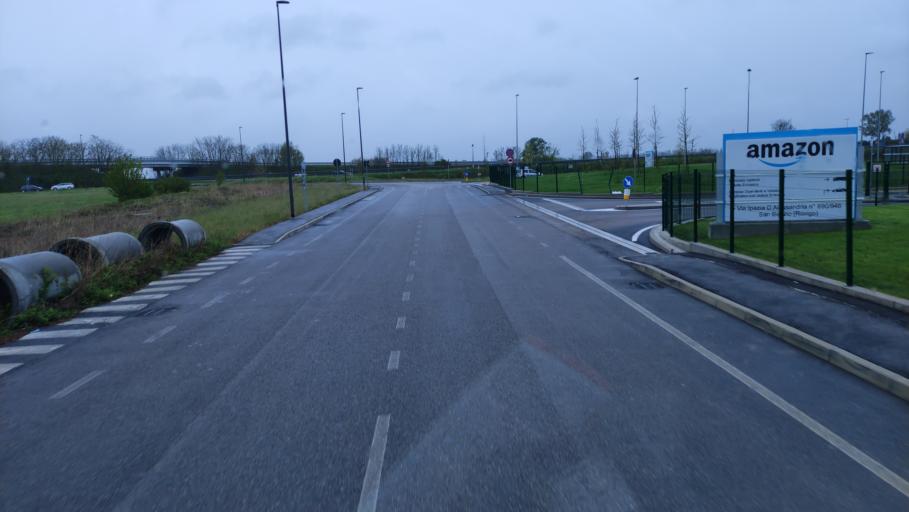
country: IT
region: Veneto
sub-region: Provincia di Rovigo
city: San Bellino
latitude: 45.0319
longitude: 11.5695
